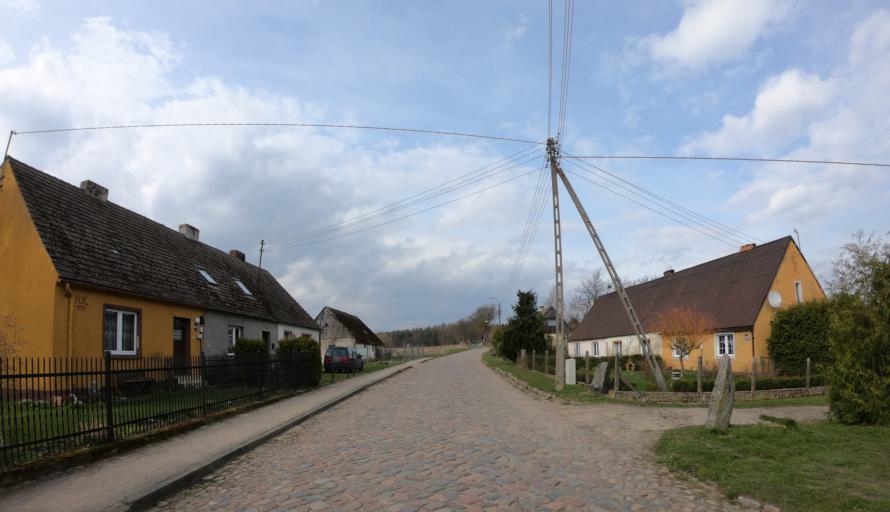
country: PL
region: West Pomeranian Voivodeship
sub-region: Powiat swidwinski
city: Swidwin
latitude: 53.8416
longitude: 15.8452
